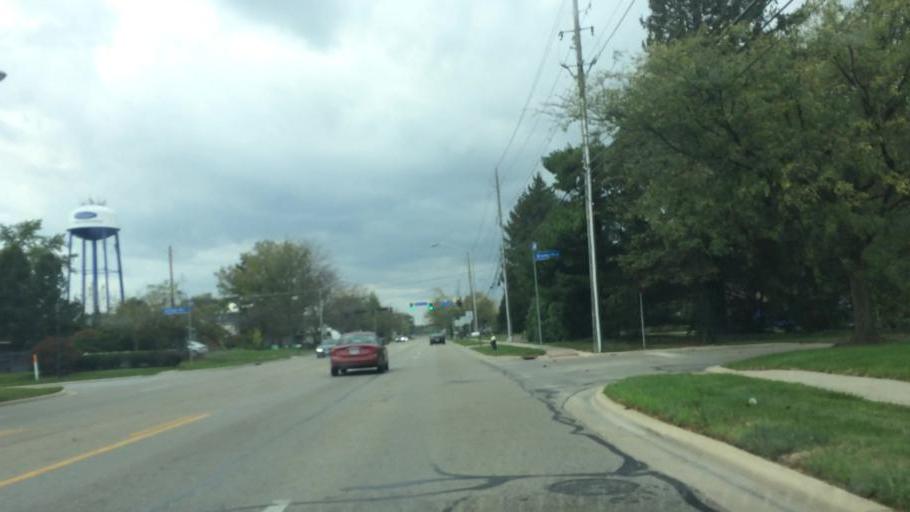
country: US
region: Ohio
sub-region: Franklin County
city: Hilliard
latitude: 40.0311
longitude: -83.1470
